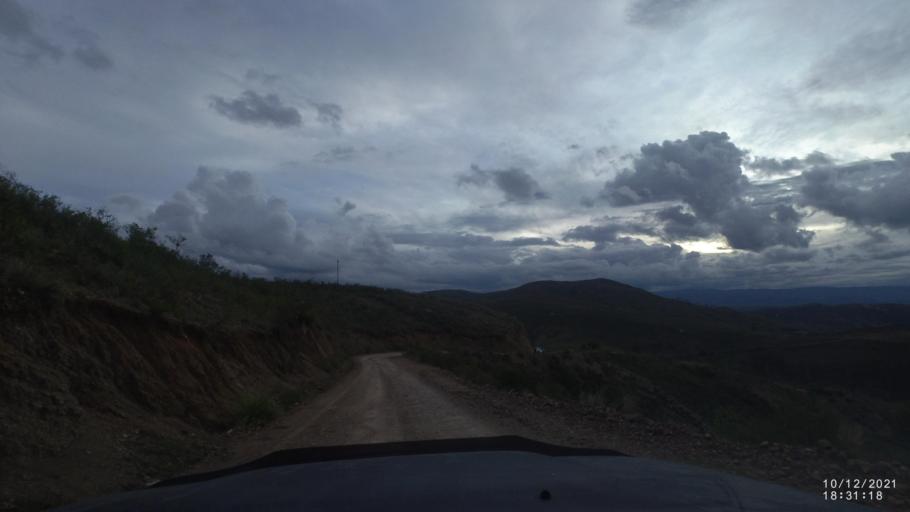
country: BO
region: Cochabamba
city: Tarata
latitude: -17.8143
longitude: -65.9837
